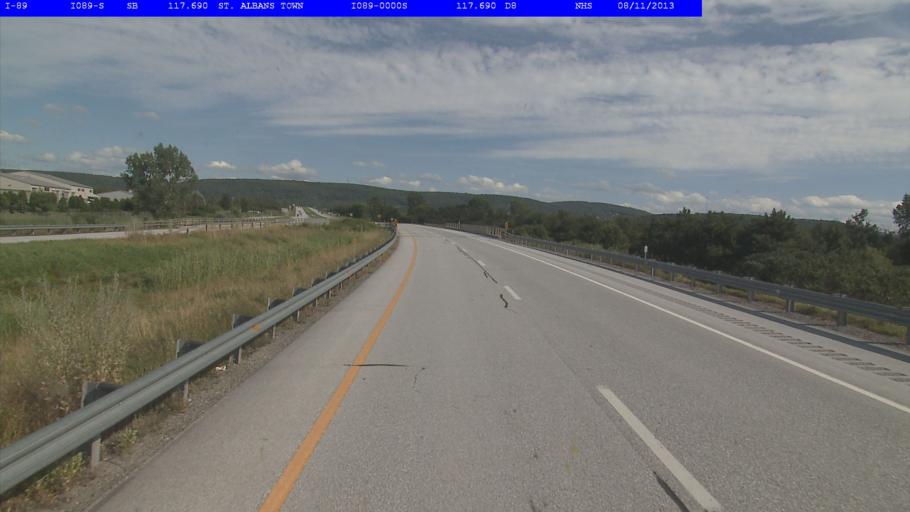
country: US
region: Vermont
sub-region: Franklin County
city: Saint Albans
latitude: 44.8442
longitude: -73.0807
